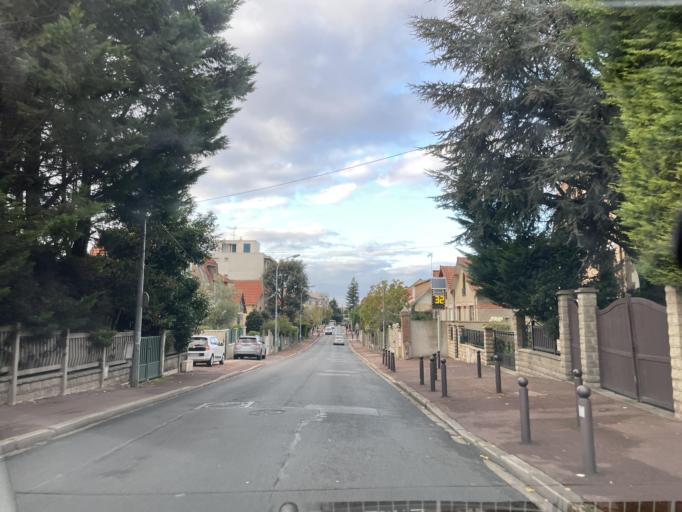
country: FR
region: Ile-de-France
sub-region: Departement du Val-de-Marne
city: Creteil
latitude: 48.7840
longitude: 2.4637
